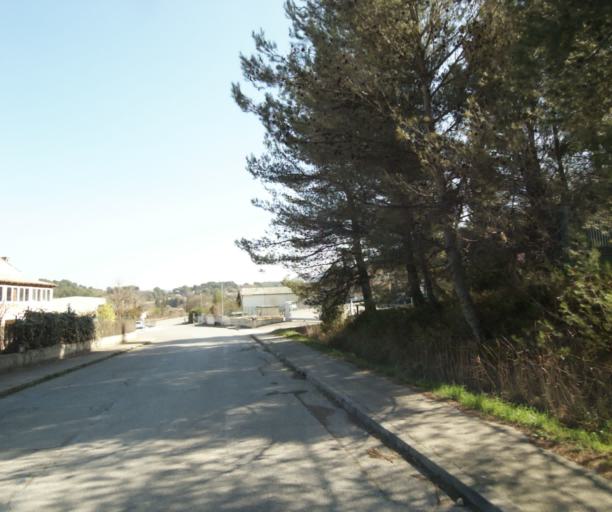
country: FR
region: Provence-Alpes-Cote d'Azur
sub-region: Departement des Bouches-du-Rhone
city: Gardanne
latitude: 43.4455
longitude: 5.4533
